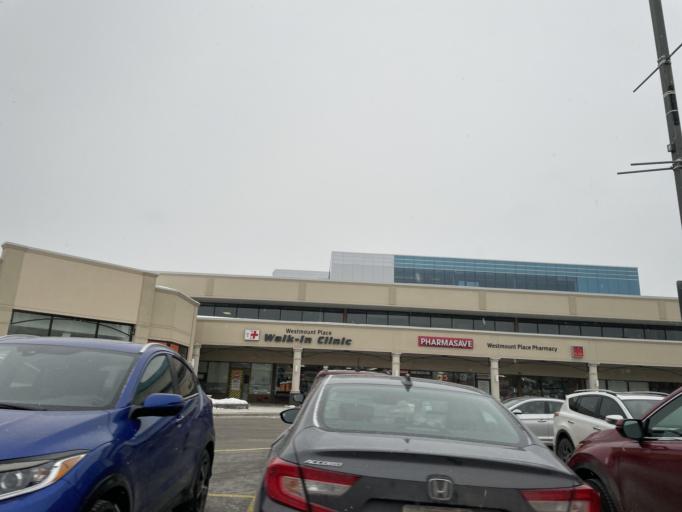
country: CA
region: Ontario
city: Waterloo
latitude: 43.4620
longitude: -80.5377
